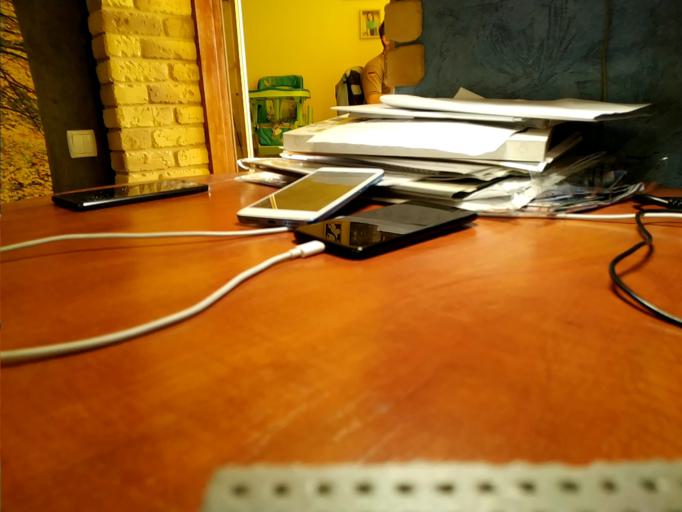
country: RU
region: Tverskaya
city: Spirovo
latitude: 57.4532
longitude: 35.0496
